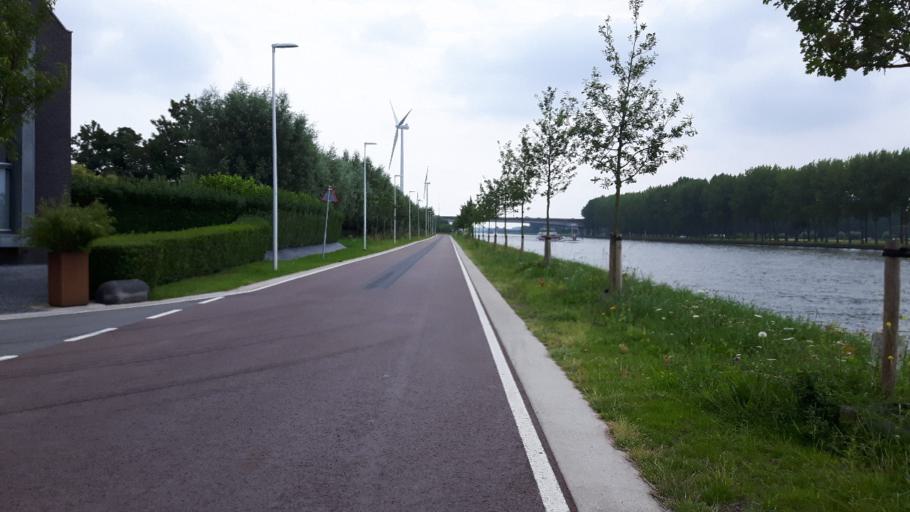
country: NL
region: Utrecht
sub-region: Gemeente Utrecht
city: Lunetten
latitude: 52.0290
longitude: 5.1252
